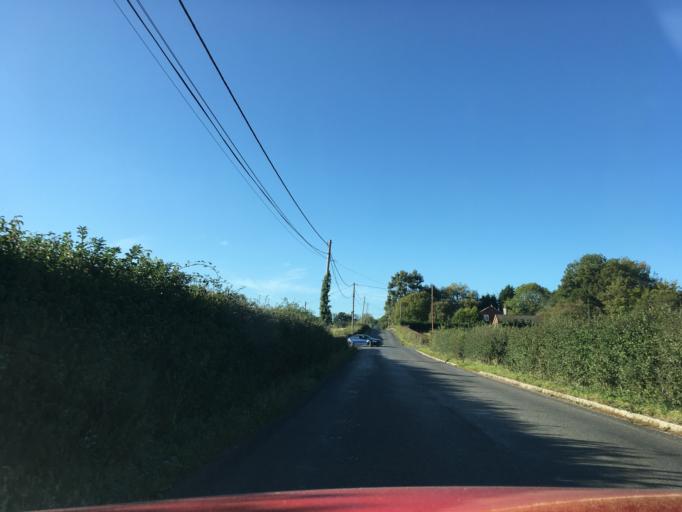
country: GB
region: England
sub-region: Hampshire
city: Swanmore
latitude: 50.9248
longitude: -1.1650
